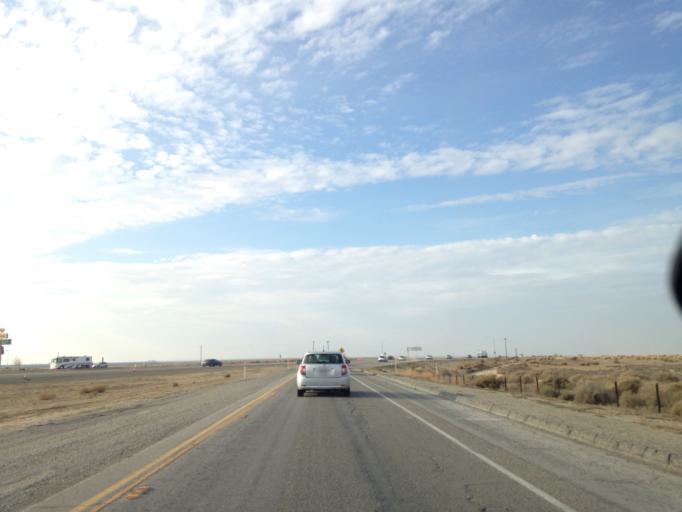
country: US
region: California
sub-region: Kern County
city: Lost Hills
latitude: 35.6177
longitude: -119.6532
